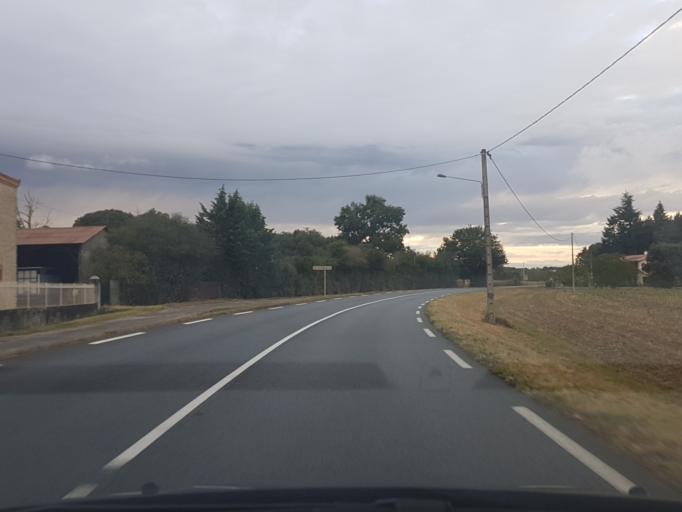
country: FR
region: Midi-Pyrenees
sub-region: Departement de l'Ariege
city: La Tour-du-Crieu
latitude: 43.0861
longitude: 1.7377
